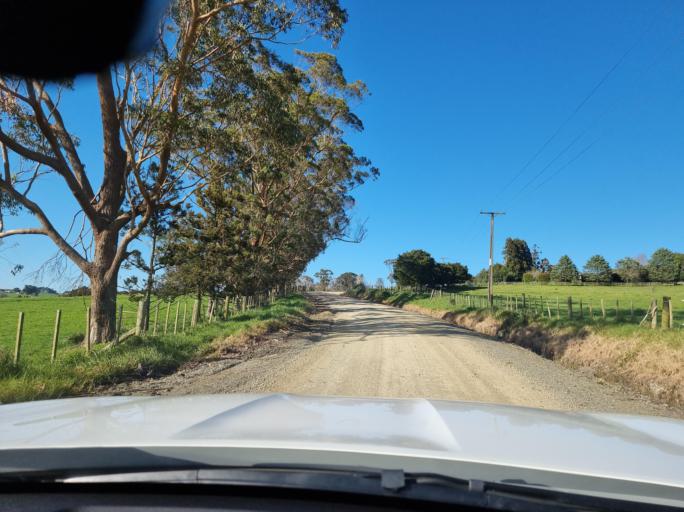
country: NZ
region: Auckland
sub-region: Auckland
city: Wellsford
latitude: -36.1653
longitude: 174.4378
